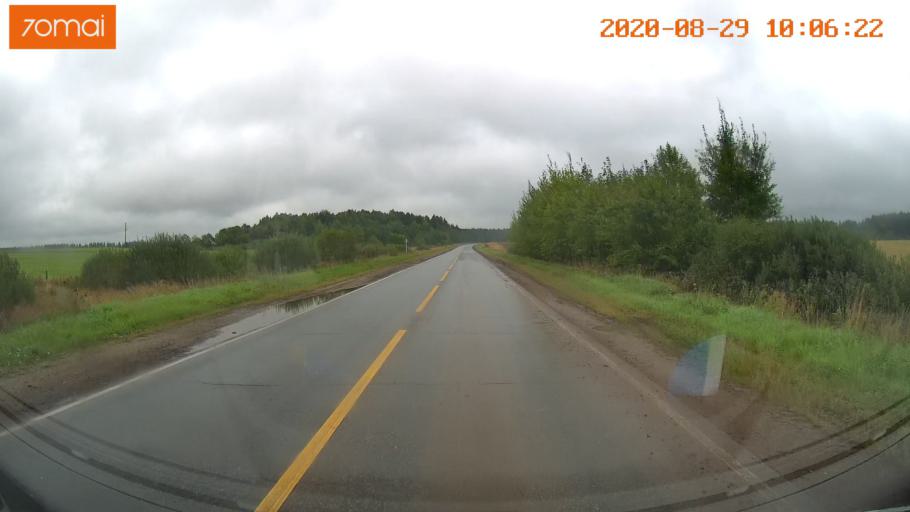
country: RU
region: Ivanovo
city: Kuznechikha
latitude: 57.3889
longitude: 42.5438
